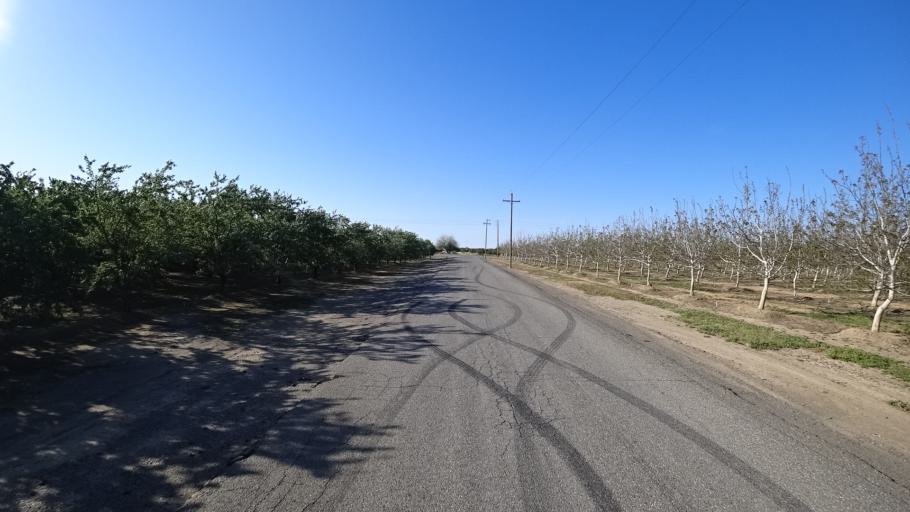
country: US
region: California
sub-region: Glenn County
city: Orland
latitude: 39.7120
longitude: -122.1598
